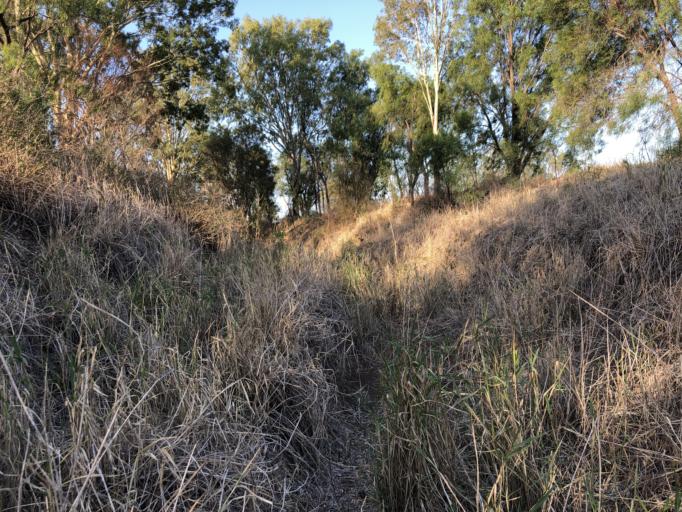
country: AU
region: Queensland
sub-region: Lockyer Valley
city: Gatton
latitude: -27.5848
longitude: 152.3473
